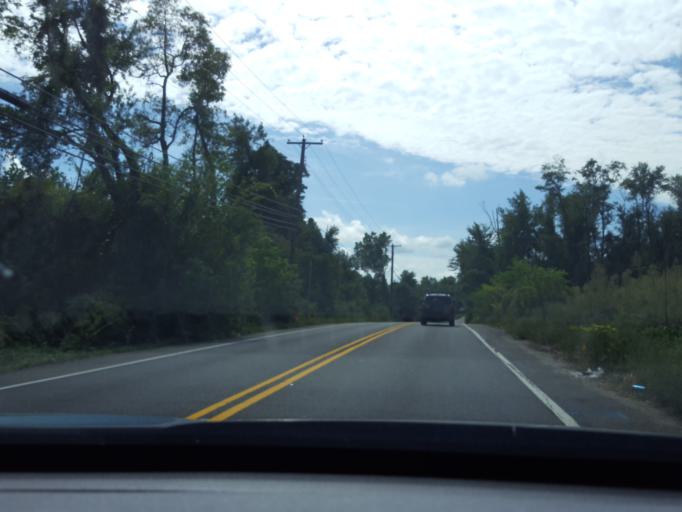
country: US
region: Maryland
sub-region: Prince George's County
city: Mellwood
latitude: 38.8070
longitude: -76.8238
